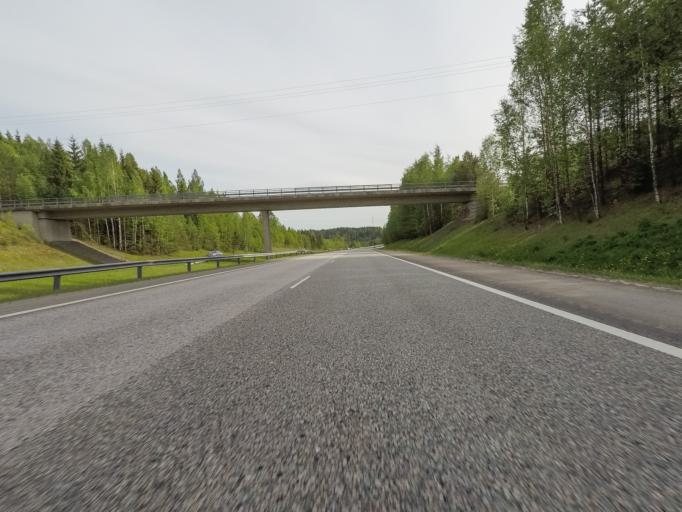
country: FI
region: Uusimaa
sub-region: Helsinki
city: Nurmijaervi
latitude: 60.4159
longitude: 24.8247
